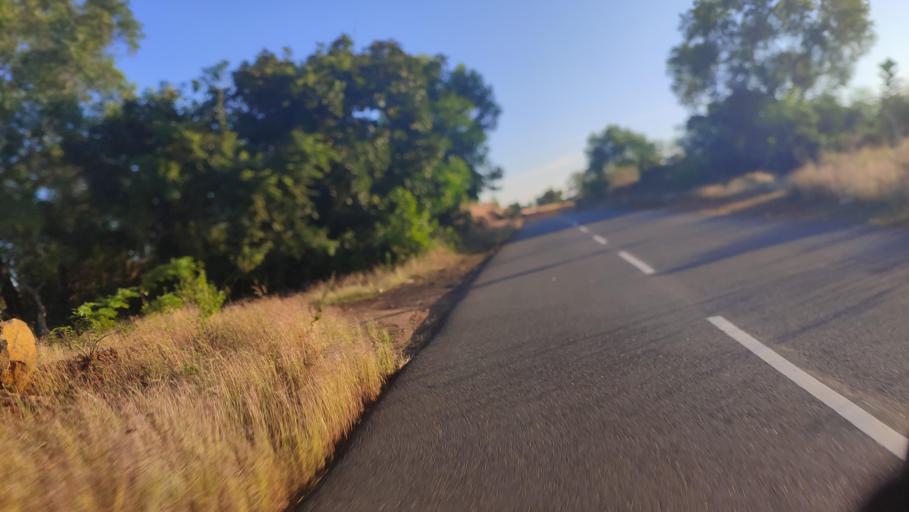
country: IN
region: Kerala
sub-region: Kasaragod District
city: Kasaragod
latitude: 12.4450
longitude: 75.0992
